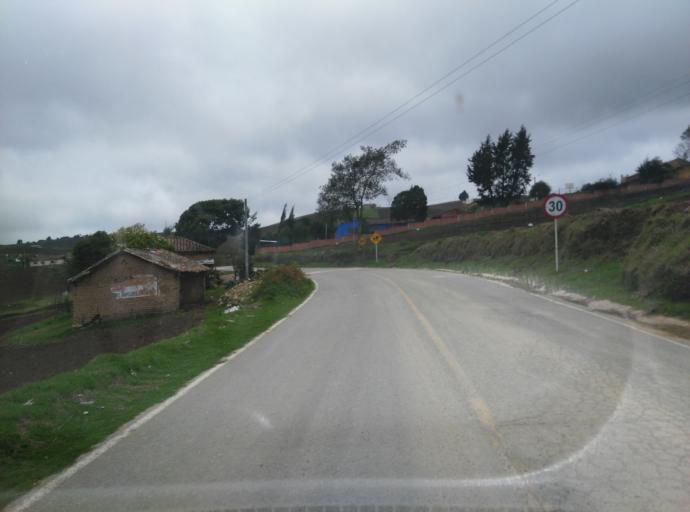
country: CO
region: Boyaca
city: Siachoque
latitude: 5.4939
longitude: -73.2792
